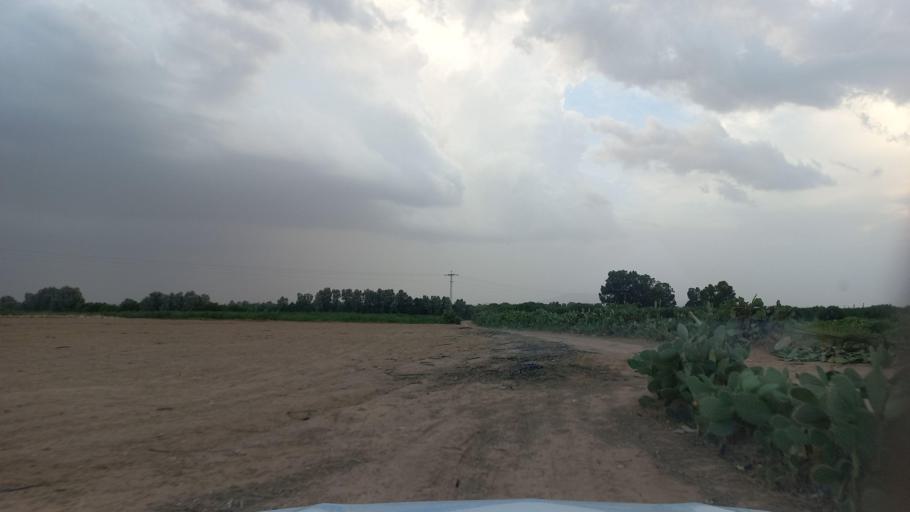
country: TN
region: Al Qasrayn
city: Kasserine
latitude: 35.2750
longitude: 9.0582
